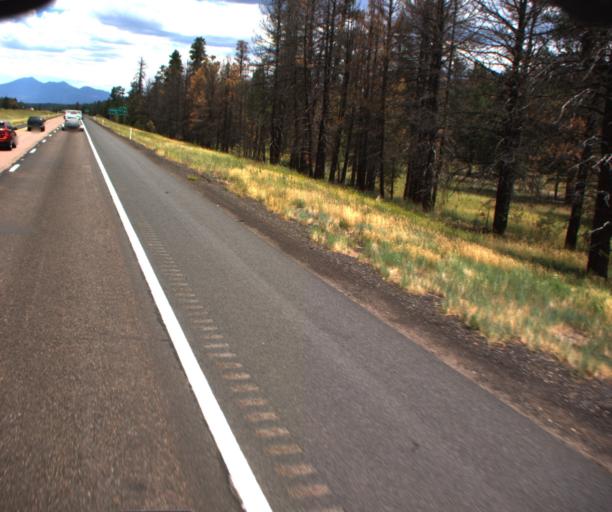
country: US
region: Arizona
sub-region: Coconino County
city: Mountainaire
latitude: 35.0121
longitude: -111.6849
